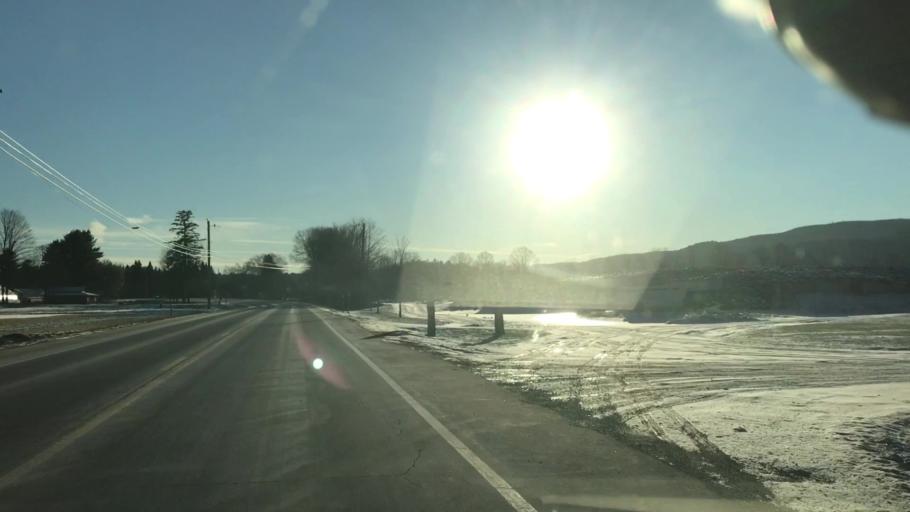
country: US
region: New Hampshire
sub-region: Grafton County
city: Orford
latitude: 43.8820
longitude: -72.1546
